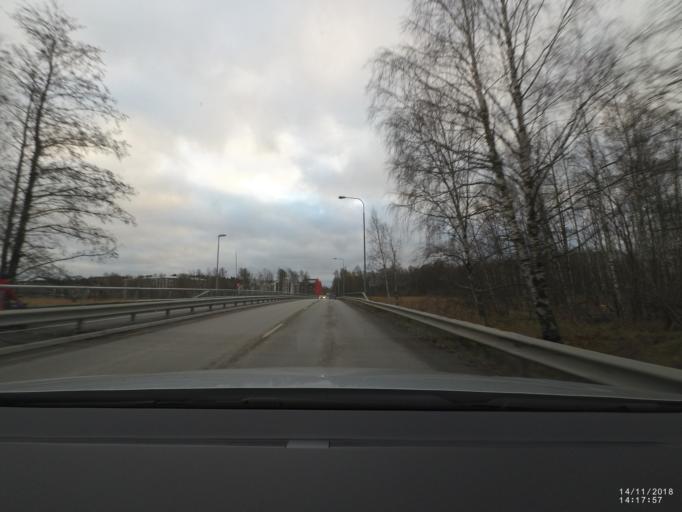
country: SE
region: Soedermanland
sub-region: Nykopings Kommun
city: Nykoping
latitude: 58.7427
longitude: 17.0061
